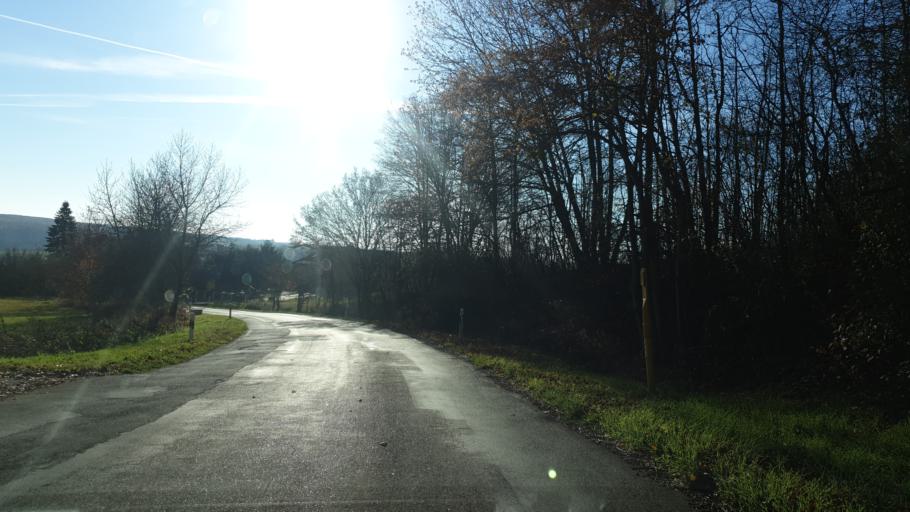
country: DE
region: Saxony-Anhalt
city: Wetterzeube
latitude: 51.0104
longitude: 12.0051
